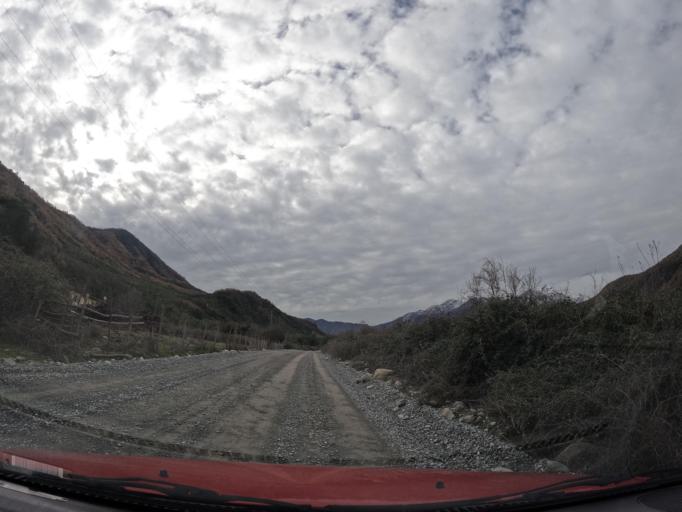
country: CL
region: Maule
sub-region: Provincia de Linares
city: Colbun
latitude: -35.8852
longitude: -71.2771
